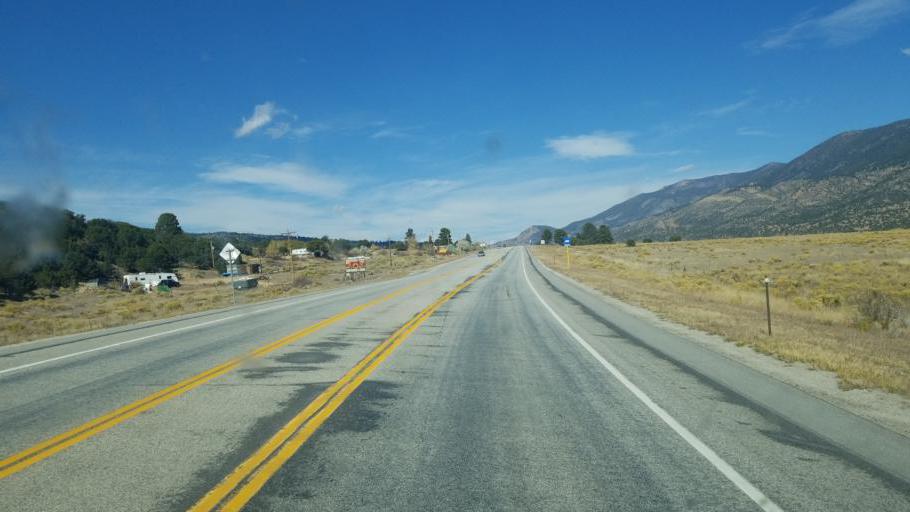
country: US
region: Colorado
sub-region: Chaffee County
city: Buena Vista
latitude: 38.9080
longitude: -106.1783
